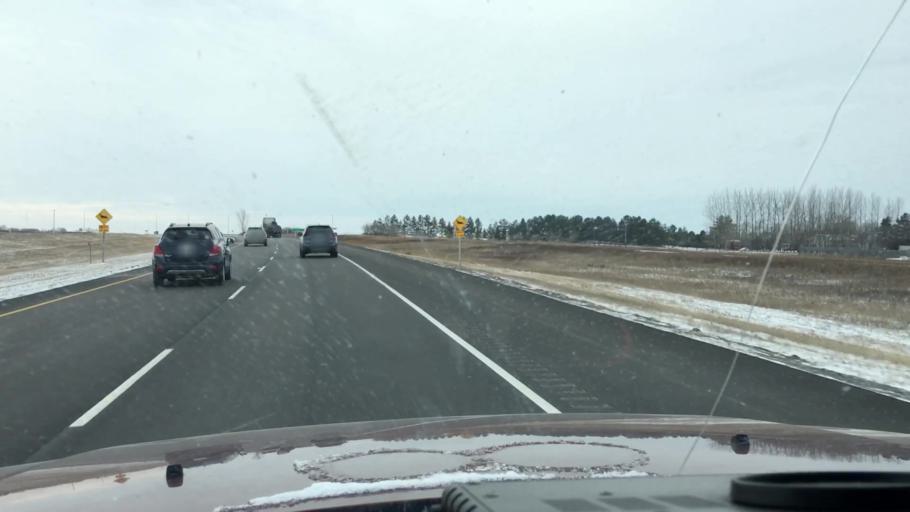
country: CA
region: Saskatchewan
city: Saskatoon
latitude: 51.8567
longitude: -106.5082
